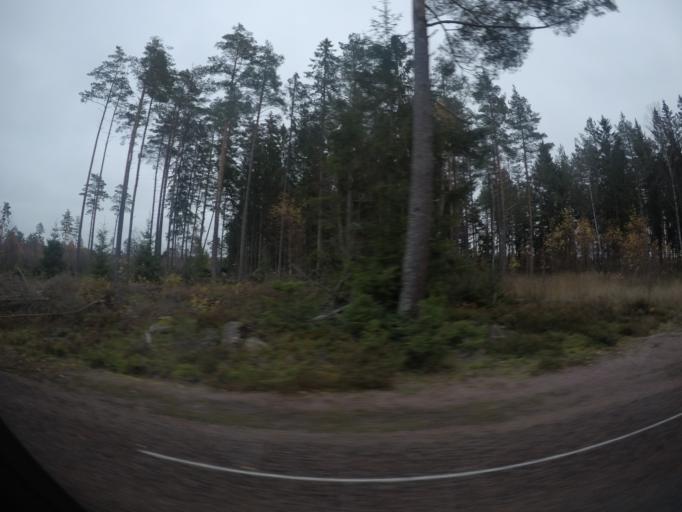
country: SE
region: Vaestmanland
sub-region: Surahammars Kommun
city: Surahammar
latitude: 59.6623
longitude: 16.0831
